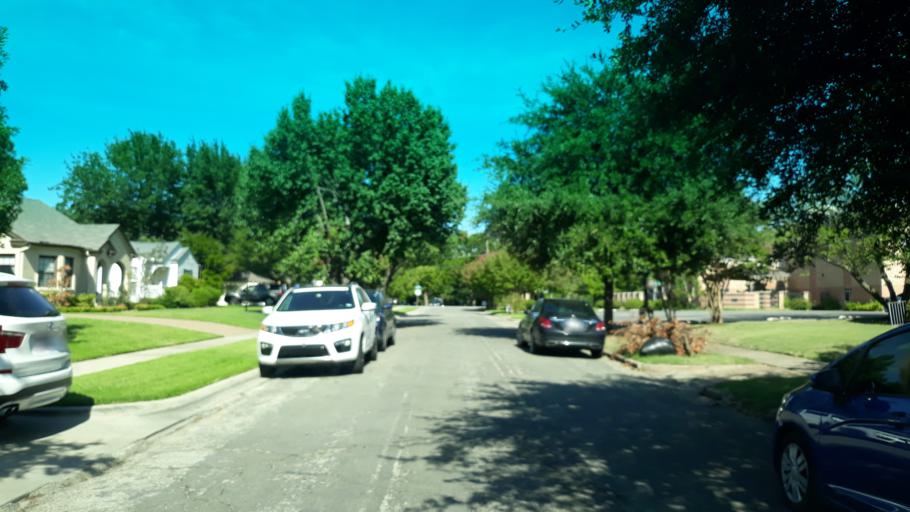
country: US
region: Texas
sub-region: Dallas County
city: Highland Park
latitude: 32.8201
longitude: -96.7541
